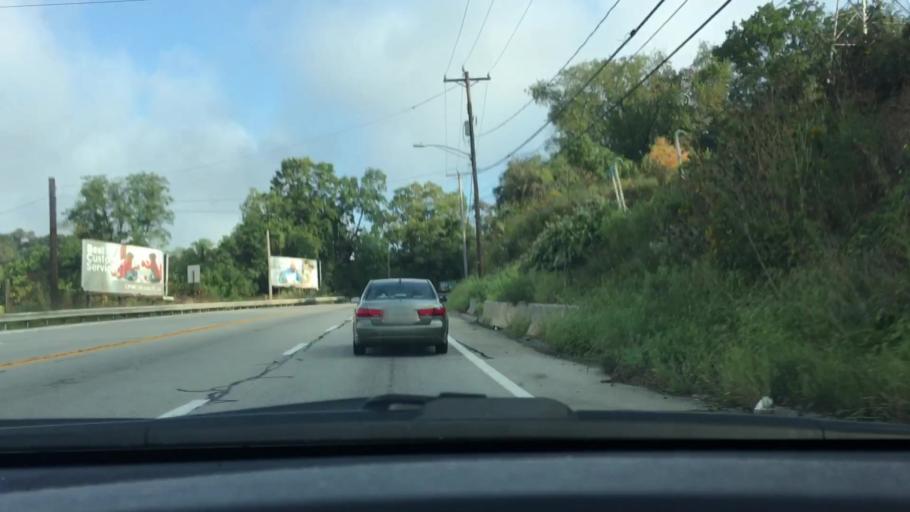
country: US
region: Pennsylvania
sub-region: Allegheny County
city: Dravosburg
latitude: 40.3515
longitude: -79.8964
